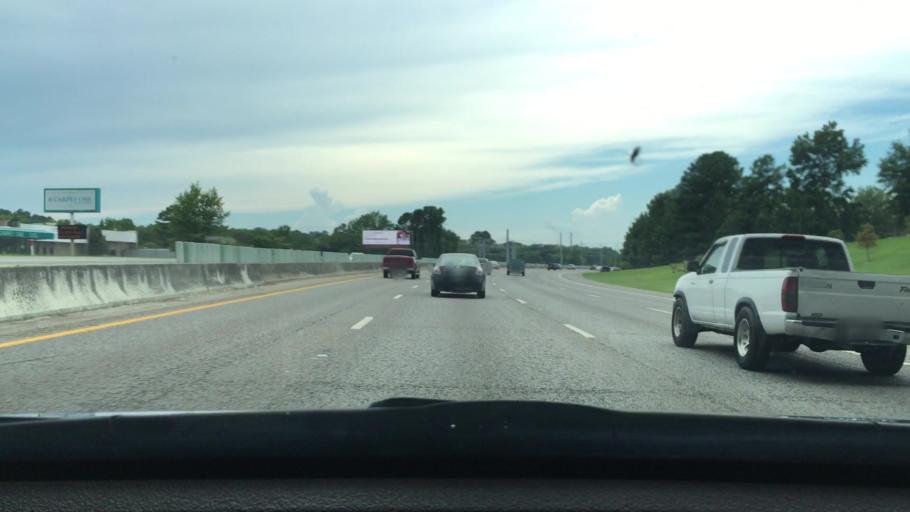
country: US
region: South Carolina
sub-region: Lexington County
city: West Columbia
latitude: 34.0126
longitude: -81.0762
